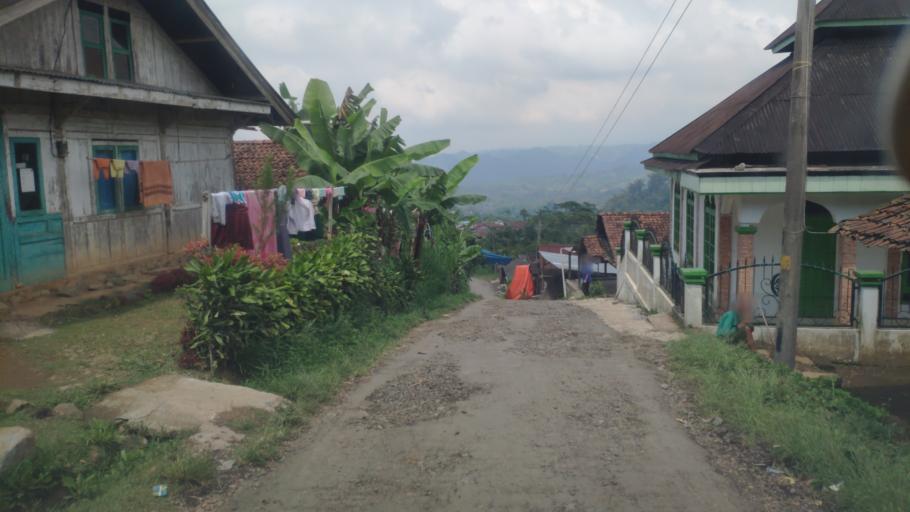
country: ID
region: Central Java
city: Wonosobo
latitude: -7.2688
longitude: 109.8089
